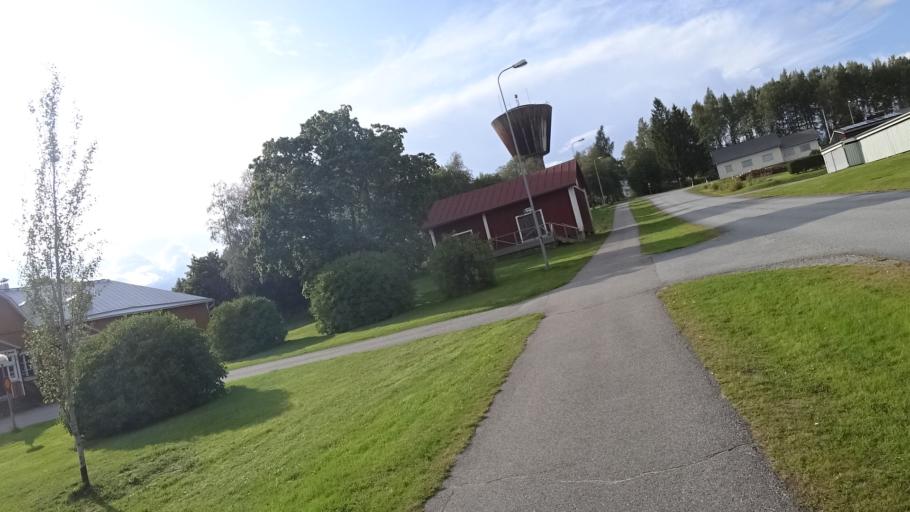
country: FI
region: North Karelia
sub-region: Joensuu
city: Ilomantsi
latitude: 62.6702
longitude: 30.9216
